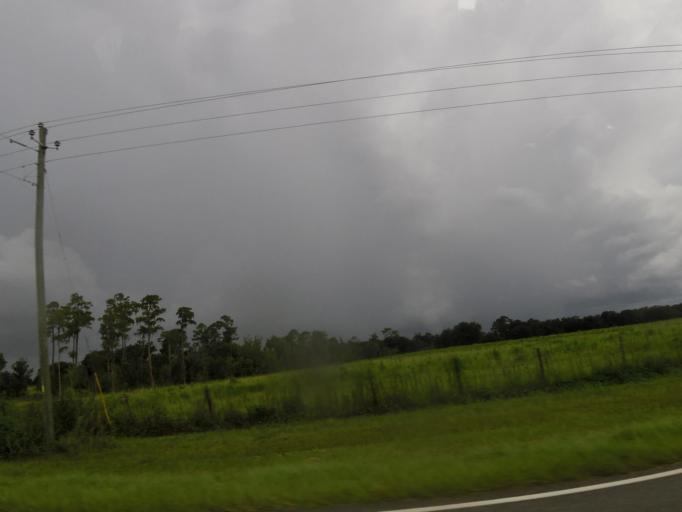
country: US
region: Florida
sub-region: Baker County
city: Macclenny
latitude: 30.4011
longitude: -82.1848
